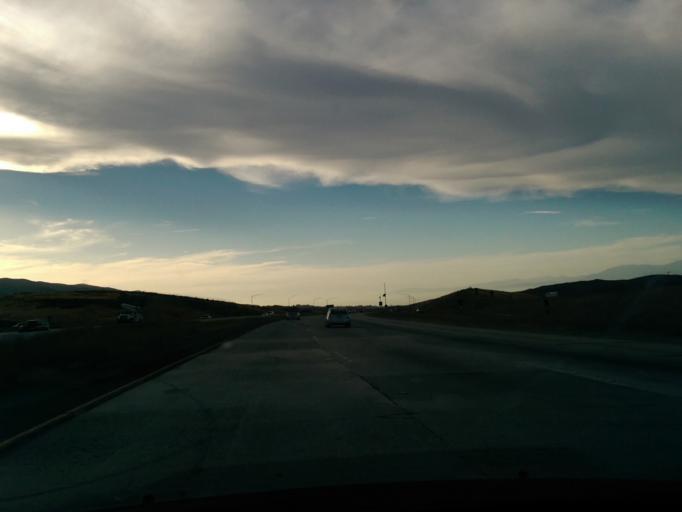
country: US
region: California
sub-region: Riverside County
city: El Cerrito
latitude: 33.7488
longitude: -117.4524
